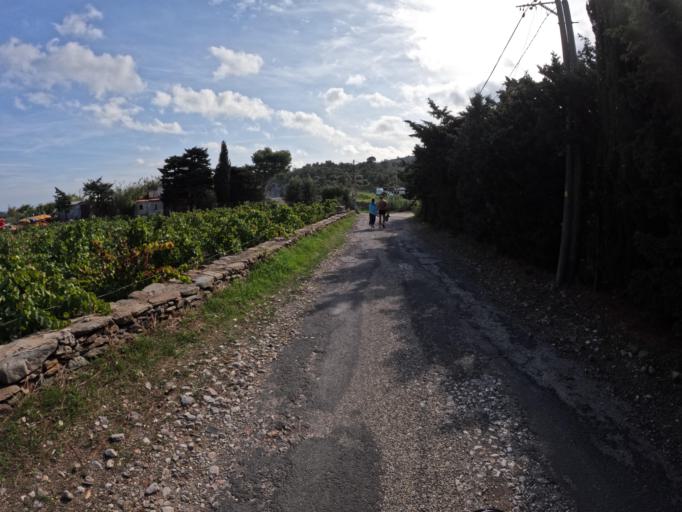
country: FR
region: Languedoc-Roussillon
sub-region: Departement des Pyrenees-Orientales
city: Cervera de la Marenda
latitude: 42.4609
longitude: 3.1558
